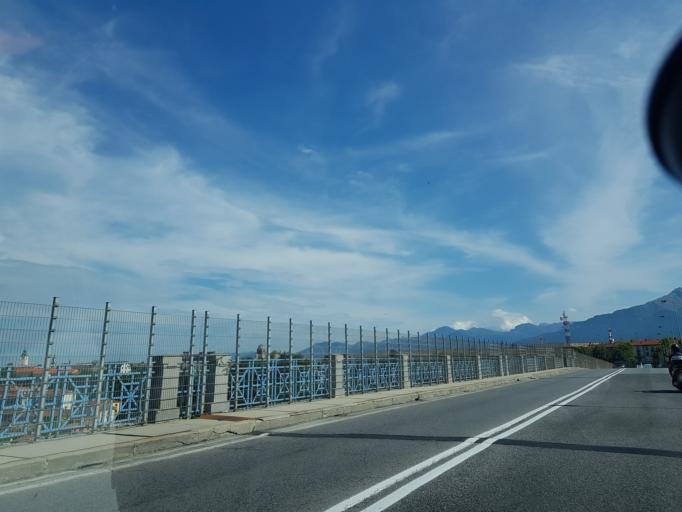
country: IT
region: Piedmont
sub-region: Provincia di Cuneo
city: Cuneo
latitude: 44.3940
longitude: 7.5410
